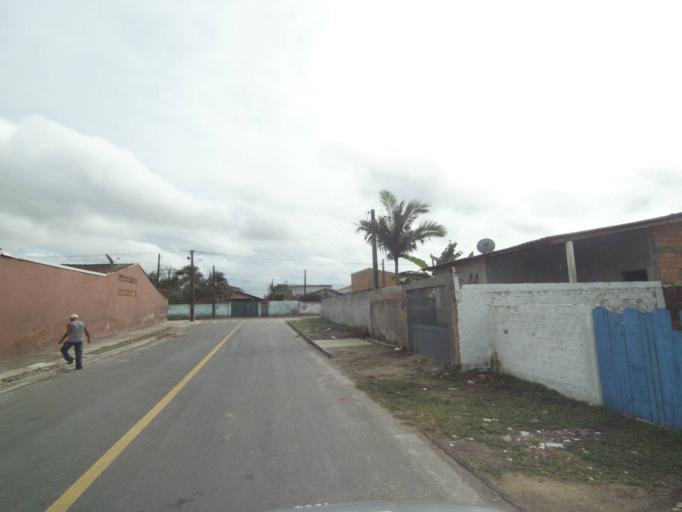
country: BR
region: Parana
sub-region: Paranagua
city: Paranagua
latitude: -25.5653
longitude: -48.5649
